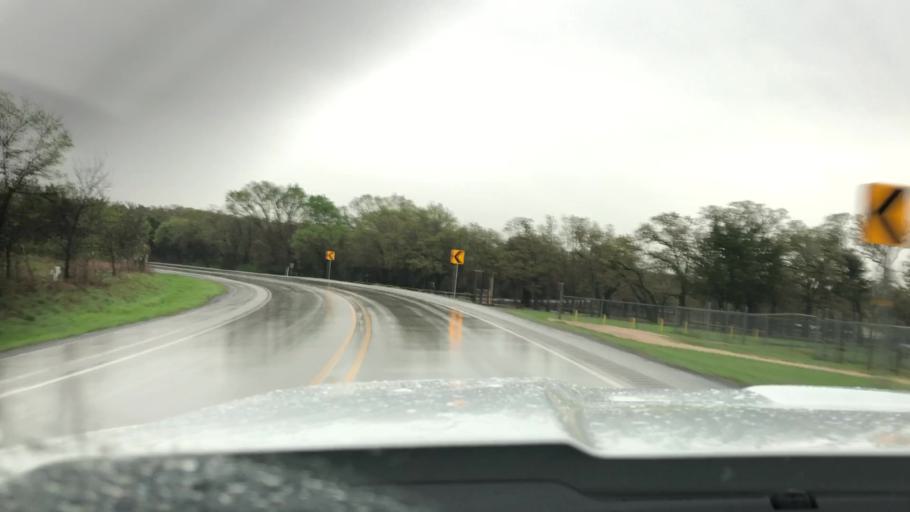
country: US
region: Texas
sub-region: Johnson County
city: Keene
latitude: 32.4531
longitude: -97.2946
